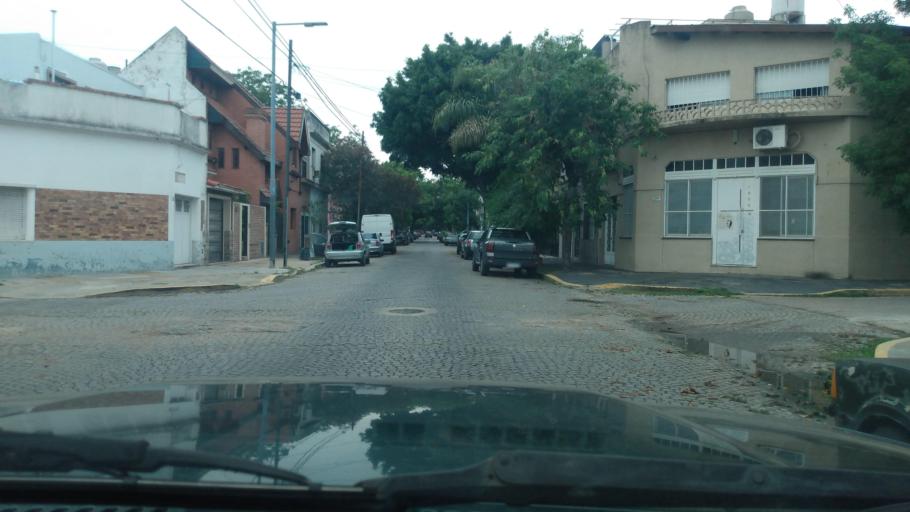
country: AR
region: Buenos Aires F.D.
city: Villa Santa Rita
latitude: -34.5860
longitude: -58.4837
